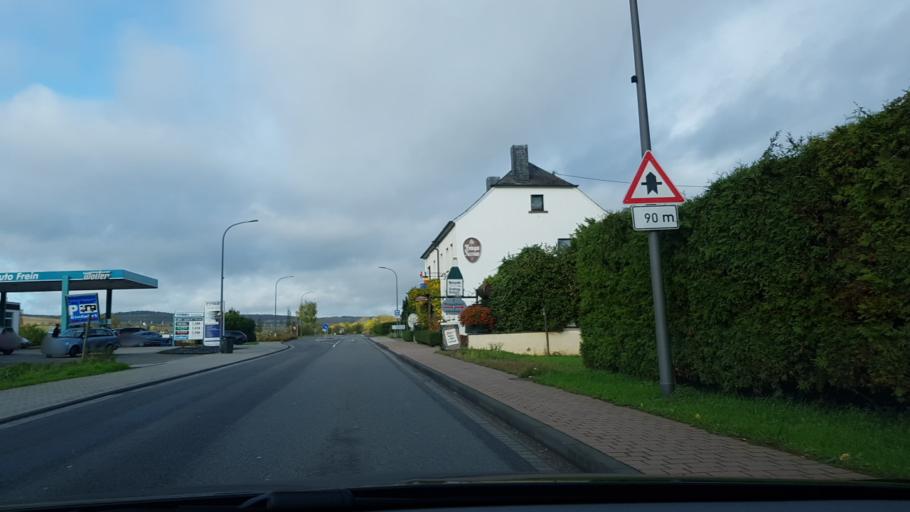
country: DE
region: Rheinland-Pfalz
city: Mehring
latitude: 49.7943
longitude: 6.8192
